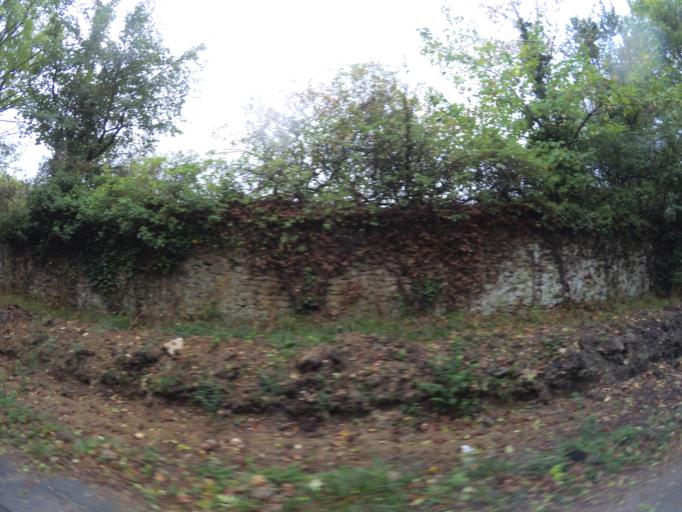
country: FR
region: Ile-de-France
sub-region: Departement de Seine-et-Marne
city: Croissy-Beaubourg
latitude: 48.8259
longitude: 2.6649
